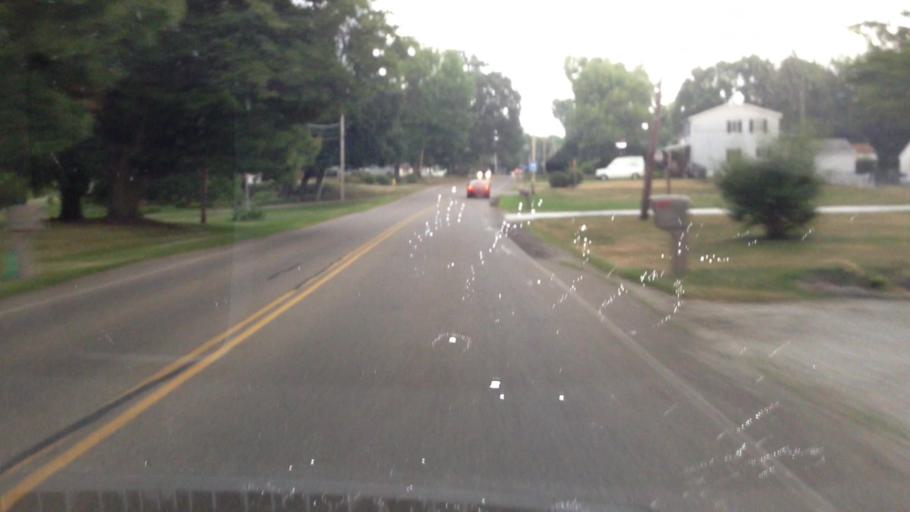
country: US
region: Ohio
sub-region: Summit County
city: Barberton
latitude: 41.0167
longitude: -81.5772
